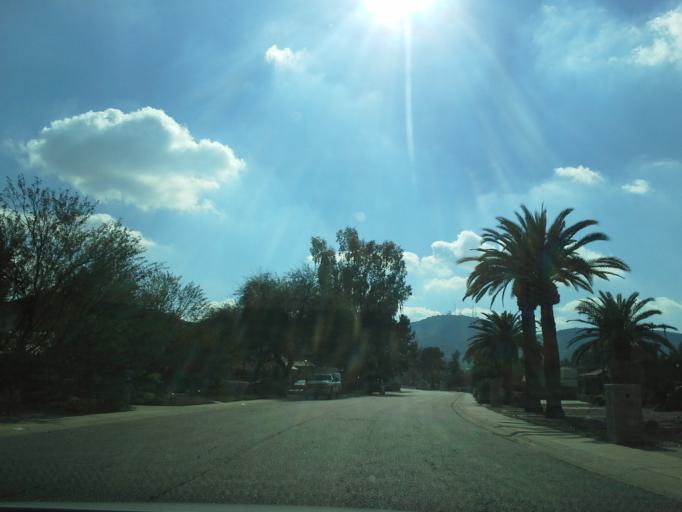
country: US
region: Arizona
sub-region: Maricopa County
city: Glendale
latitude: 33.6156
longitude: -112.0823
